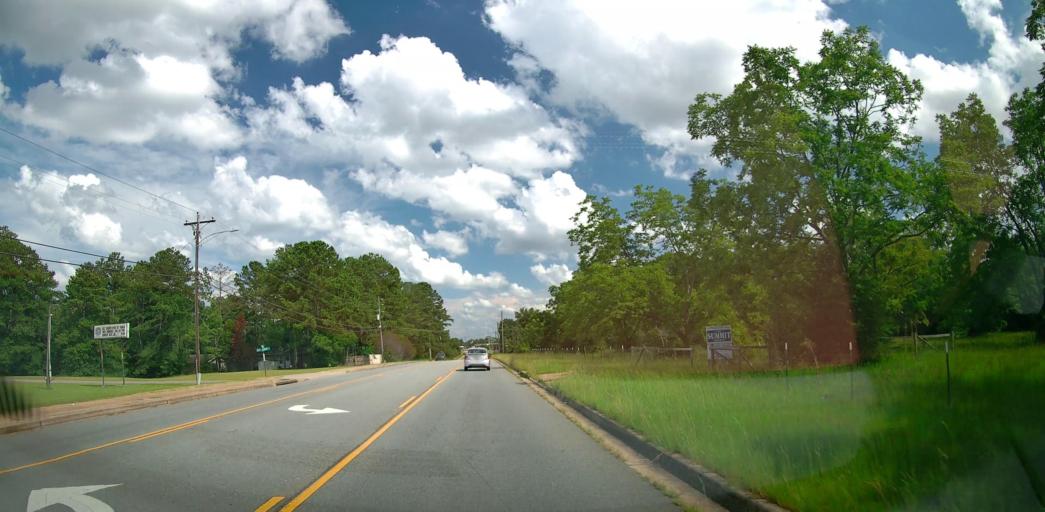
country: US
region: Georgia
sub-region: Houston County
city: Centerville
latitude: 32.5999
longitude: -83.6595
